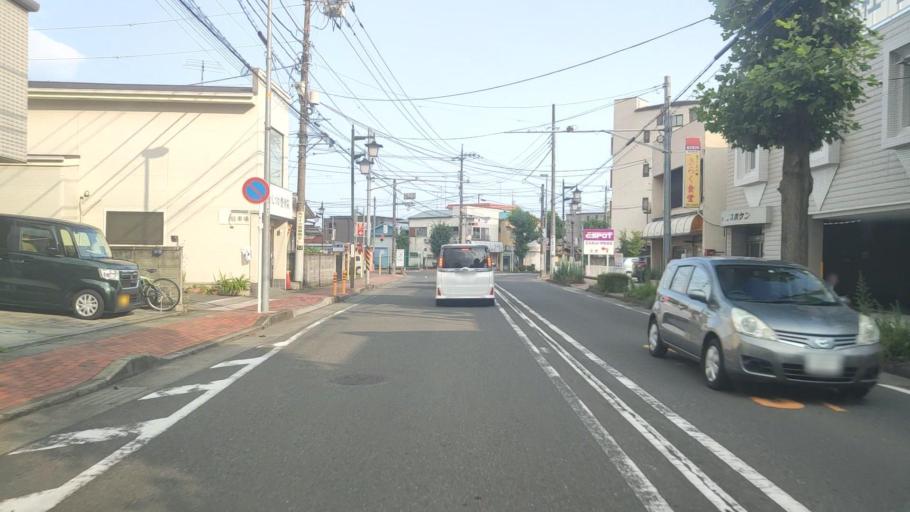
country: JP
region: Kanagawa
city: Isehara
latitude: 35.3931
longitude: 139.3141
